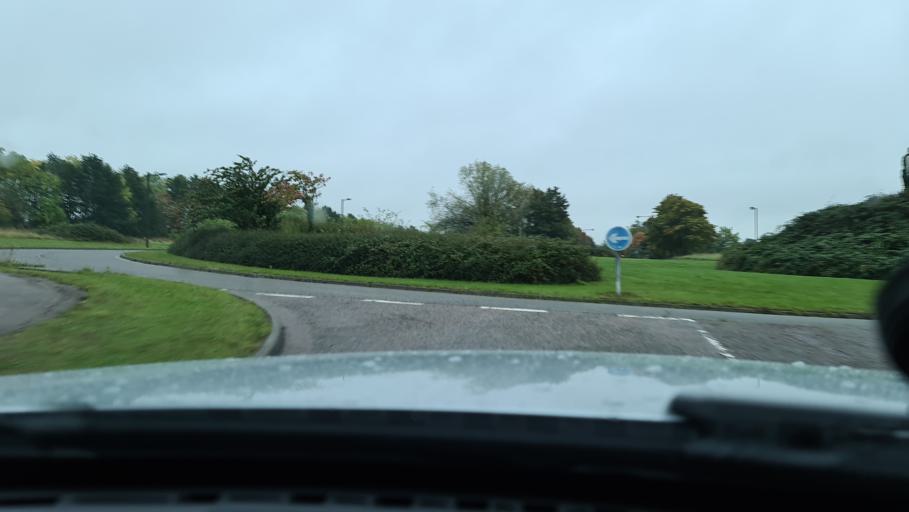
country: GB
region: England
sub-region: Milton Keynes
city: Simpson
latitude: 52.0257
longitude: -0.7007
